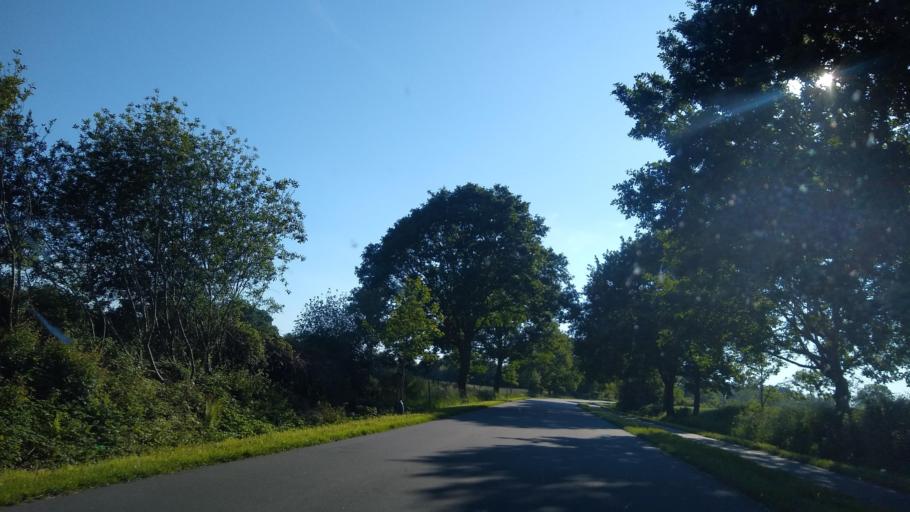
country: DE
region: Schleswig-Holstein
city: Neudorf-Bornstein
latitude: 54.4119
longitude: 9.9545
